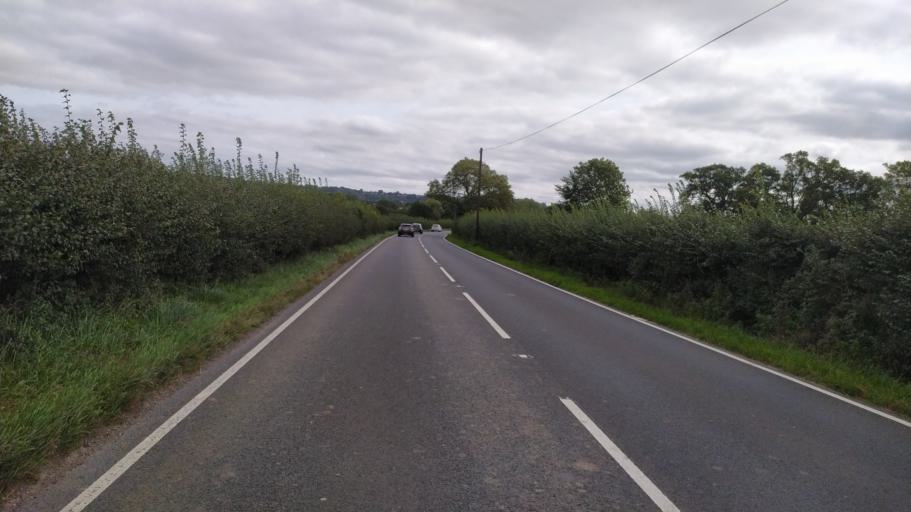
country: GB
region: England
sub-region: Dorset
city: Gillingham
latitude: 51.0213
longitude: -2.2444
